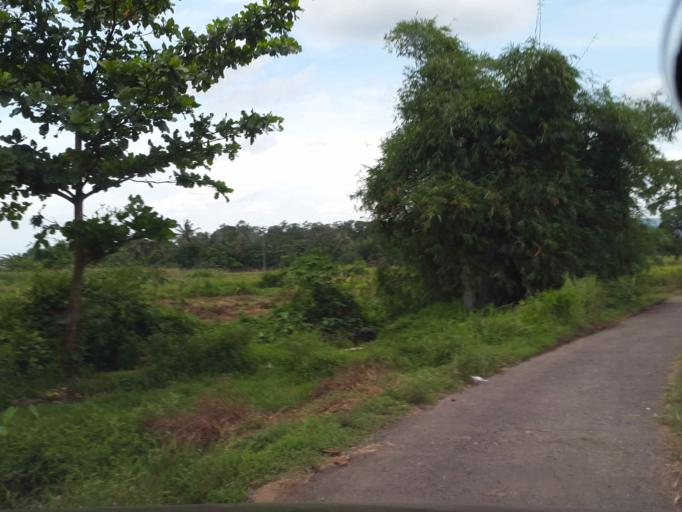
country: ID
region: West Nusa Tenggara
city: Karang Kuripan
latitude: -8.6415
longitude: 116.1704
